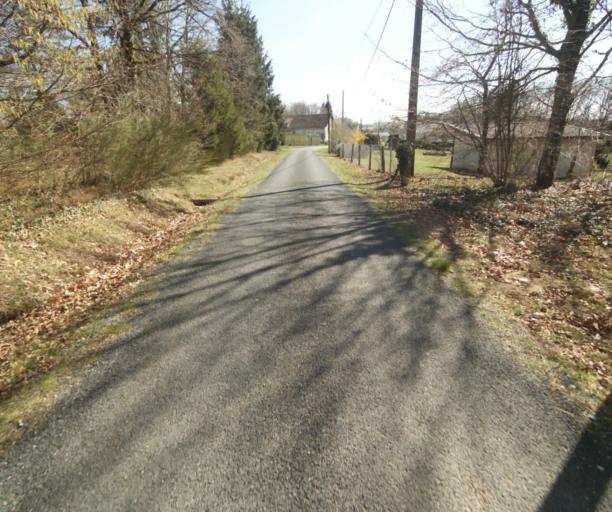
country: FR
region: Limousin
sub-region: Departement de la Correze
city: Saint-Clement
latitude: 45.3120
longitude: 1.6782
